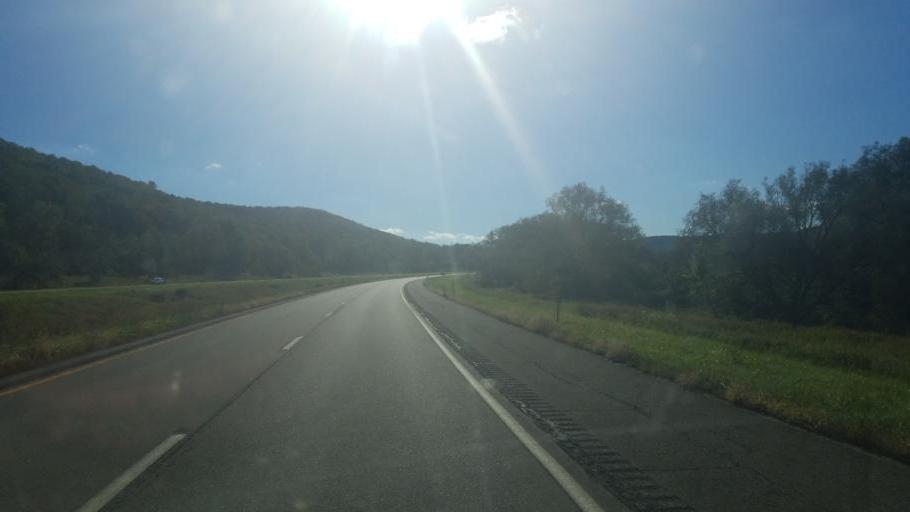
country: US
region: New York
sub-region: Allegany County
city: Cuba
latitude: 42.1844
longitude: -78.3483
